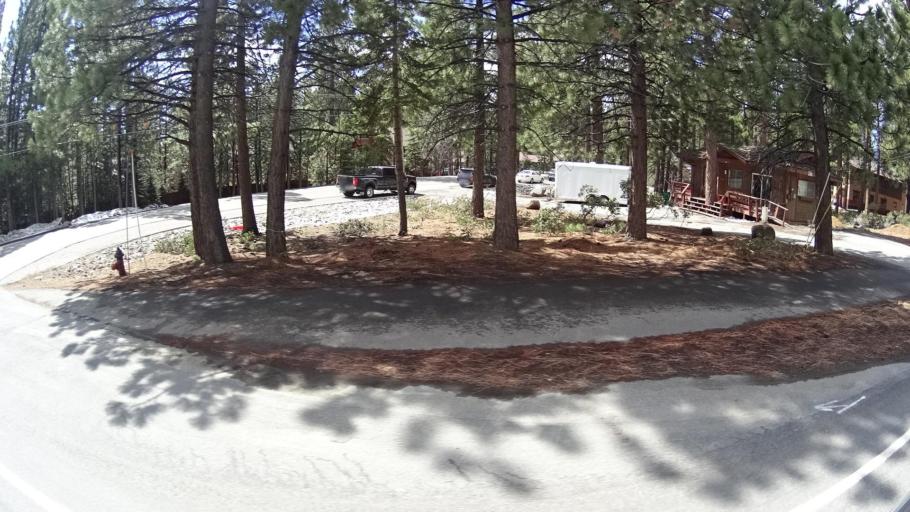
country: US
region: Nevada
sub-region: Washoe County
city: Incline Village
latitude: 39.2465
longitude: -119.9515
